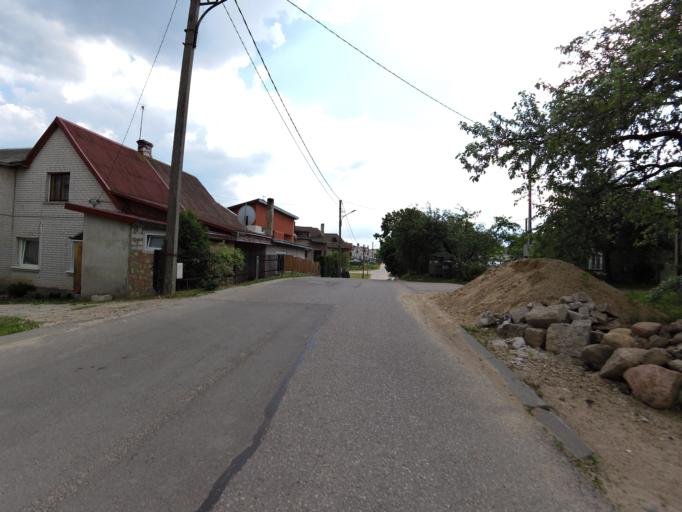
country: LT
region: Vilnius County
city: Seskine
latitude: 54.7238
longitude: 25.2772
